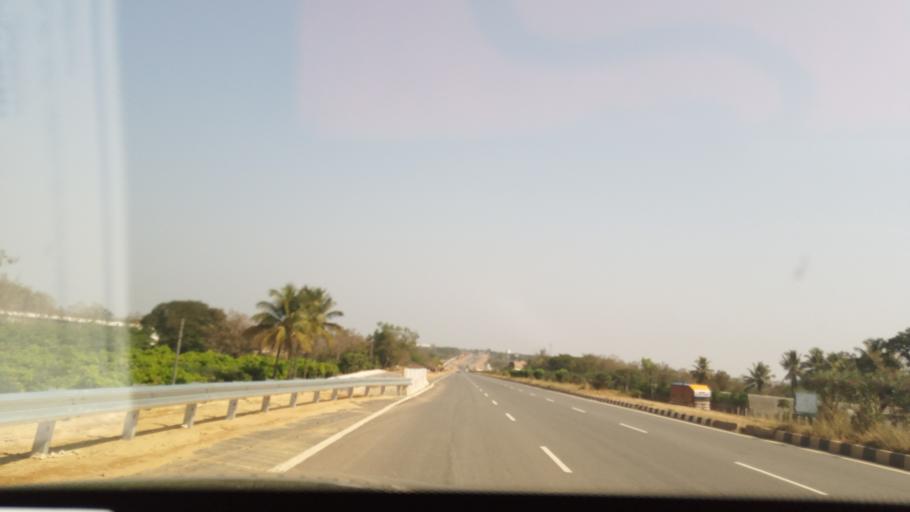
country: IN
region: Karnataka
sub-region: Dharwad
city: Kundgol
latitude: 15.2356
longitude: 75.1414
